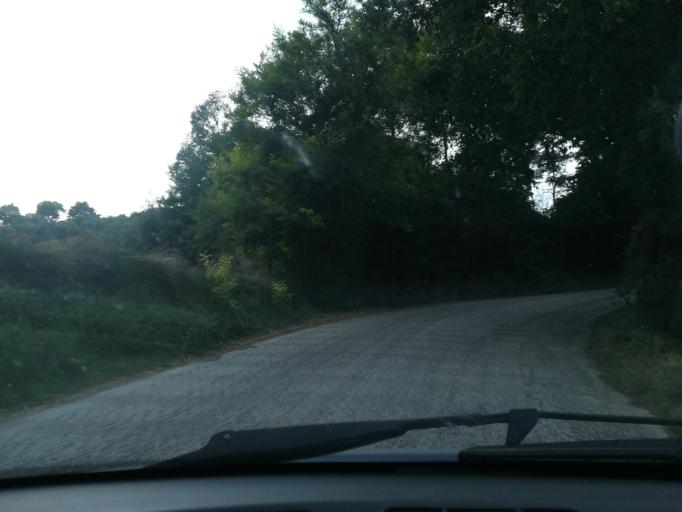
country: IT
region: The Marches
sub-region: Provincia di Macerata
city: Macerata
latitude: 43.3083
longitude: 13.4678
